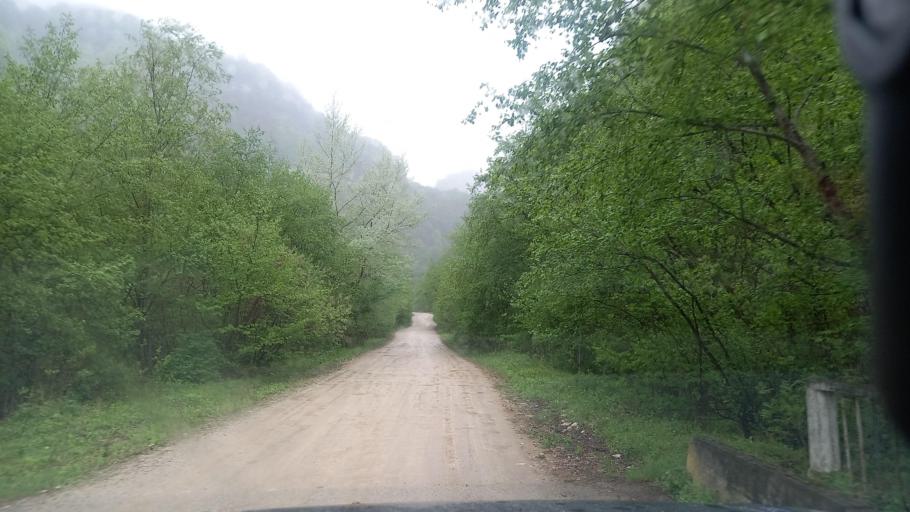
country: RU
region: Kabardino-Balkariya
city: Gundelen
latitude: 43.5885
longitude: 43.1219
